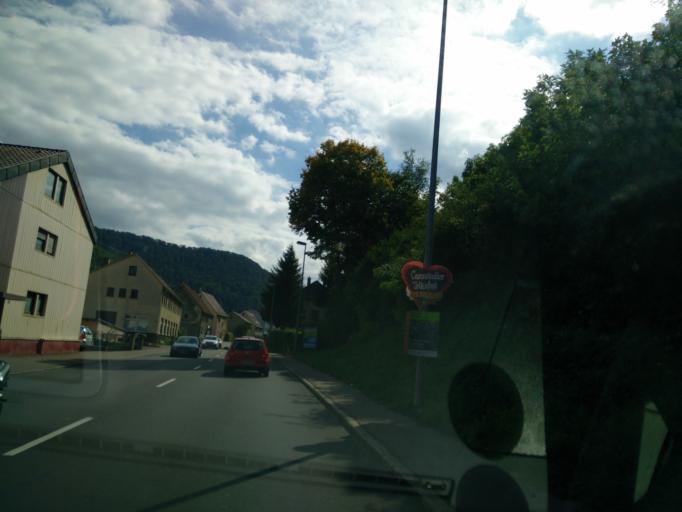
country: DE
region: Baden-Wuerttemberg
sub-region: Tuebingen Region
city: Pfullingen
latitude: 48.4371
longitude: 9.2543
